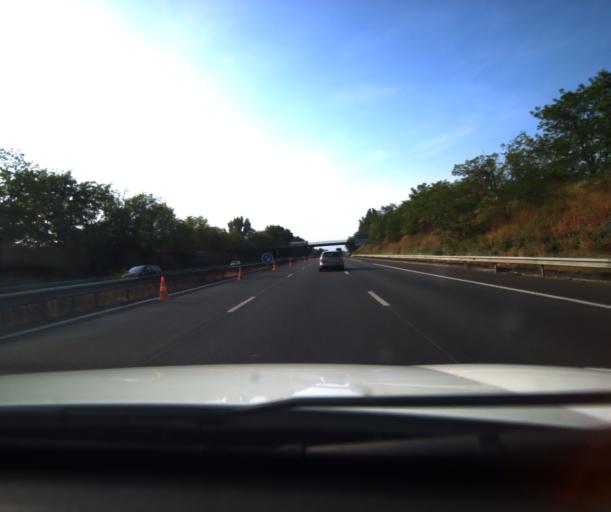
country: FR
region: Midi-Pyrenees
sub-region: Departement de la Haute-Garonne
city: Aucamville
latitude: 43.6761
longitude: 1.4157
